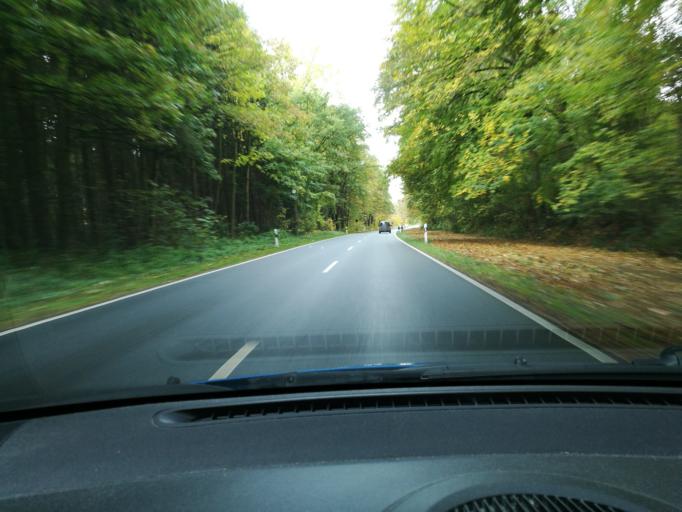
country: DE
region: Schleswig-Holstein
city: Gross Gronau
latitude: 53.7796
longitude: 10.7494
